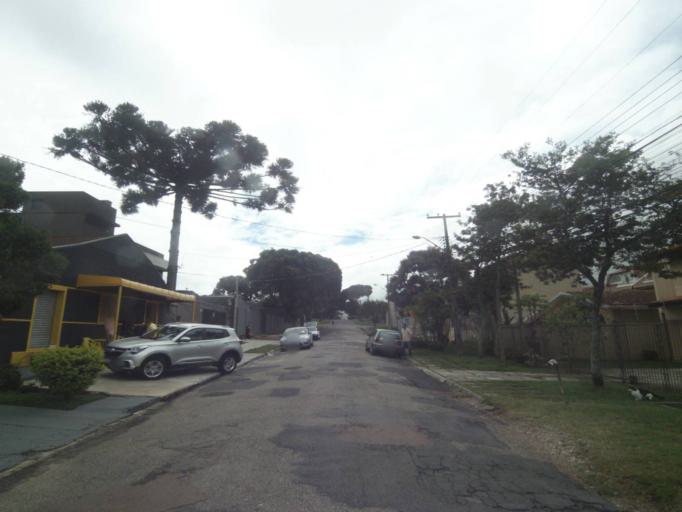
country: BR
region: Parana
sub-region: Curitiba
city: Curitiba
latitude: -25.4863
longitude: -49.3033
